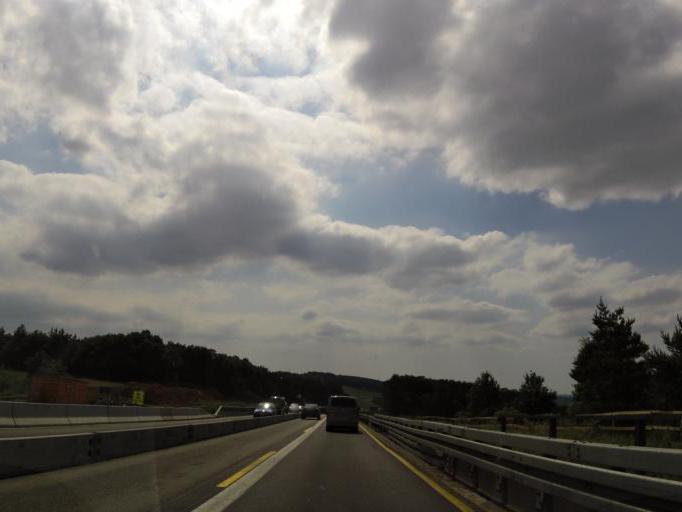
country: DE
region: Bavaria
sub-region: Regierungsbezirk Unterfranken
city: Holzkirchen
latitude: 49.7645
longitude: 9.6497
